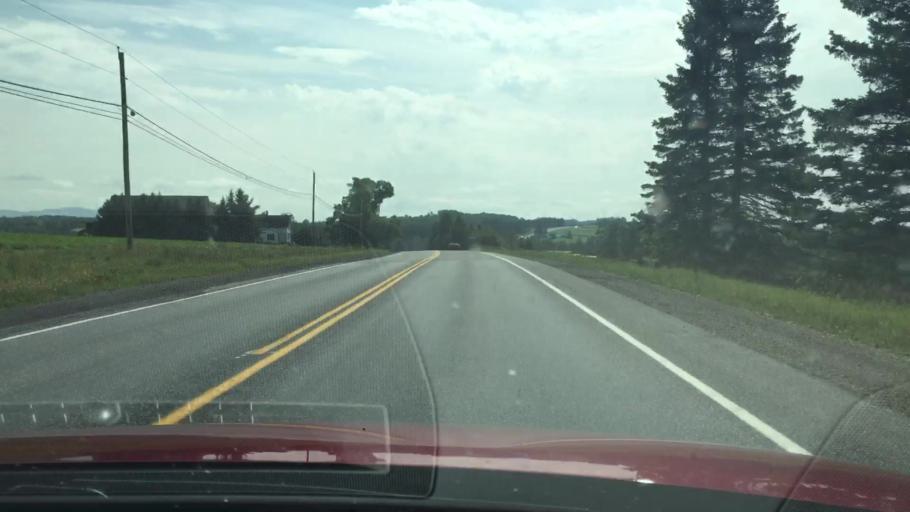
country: US
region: Maine
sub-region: Aroostook County
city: Easton
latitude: 46.6046
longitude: -67.9738
